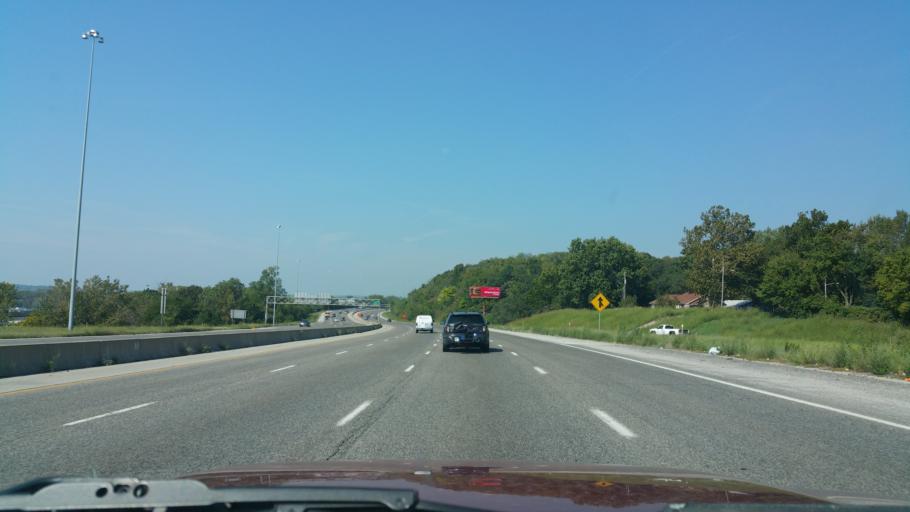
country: US
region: Kansas
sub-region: Wyandotte County
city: Kansas City
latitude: 39.0965
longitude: -94.6506
